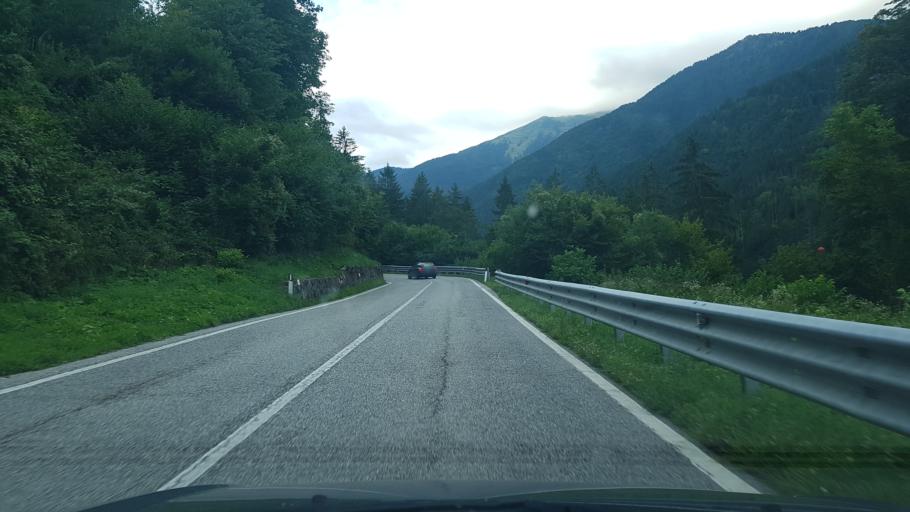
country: IT
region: Friuli Venezia Giulia
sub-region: Provincia di Udine
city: Comeglians
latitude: 46.5280
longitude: 12.8699
